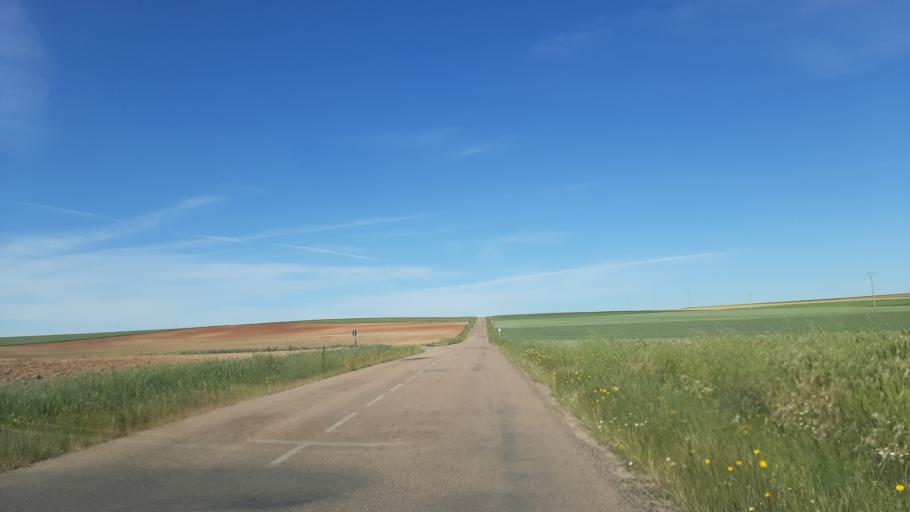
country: ES
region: Castille and Leon
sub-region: Provincia de Salamanca
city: Aldeaseca de Alba
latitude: 40.8186
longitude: -5.4523
